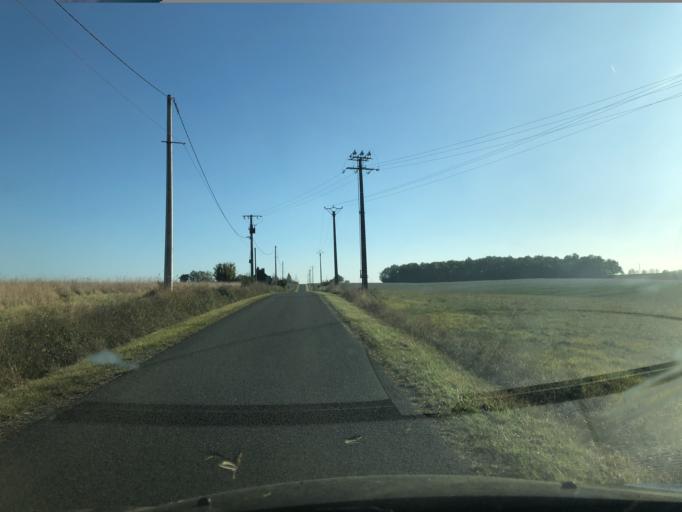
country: FR
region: Centre
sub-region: Departement d'Indre-et-Loire
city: Neuvy-le-Roi
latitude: 47.6528
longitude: 0.6115
